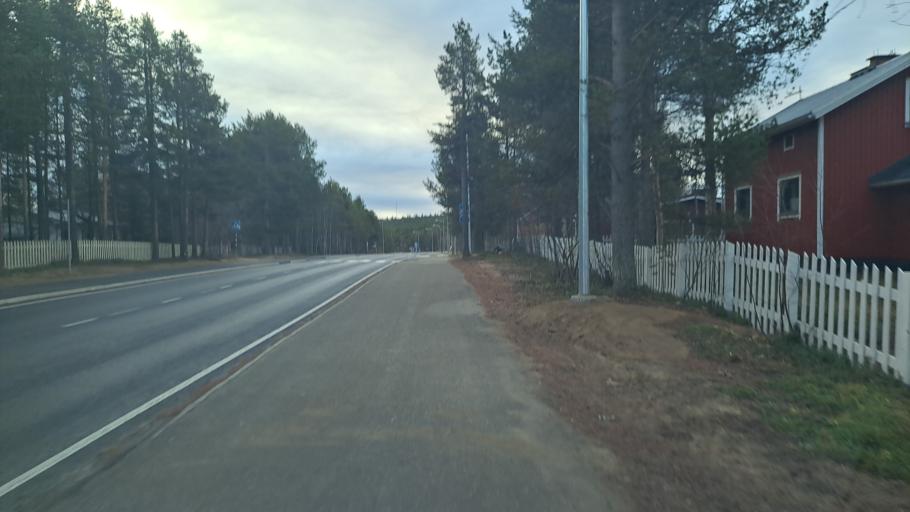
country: FI
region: Lapland
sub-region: Pohjois-Lappi
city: Inari
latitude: 68.9049
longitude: 27.0308
